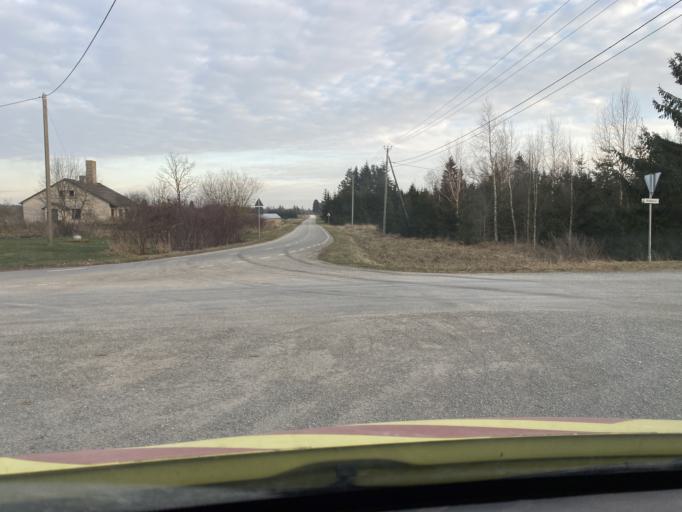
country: EE
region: Jogevamaa
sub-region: Poltsamaa linn
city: Poltsamaa
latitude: 58.5943
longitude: 26.0021
